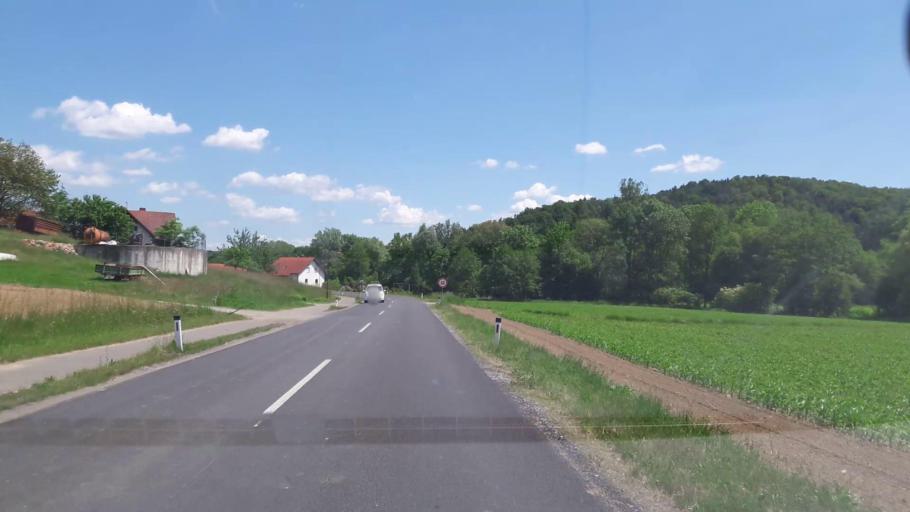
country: AT
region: Styria
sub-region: Politischer Bezirk Suedoststeiermark
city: Unterlamm
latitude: 46.9617
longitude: 16.0981
